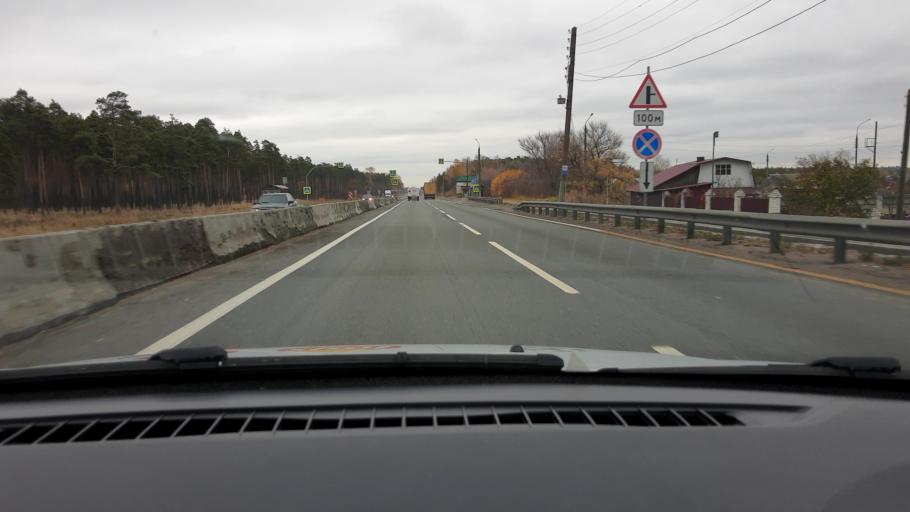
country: RU
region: Nizjnij Novgorod
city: Dzerzhinsk
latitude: 56.2977
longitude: 43.4601
